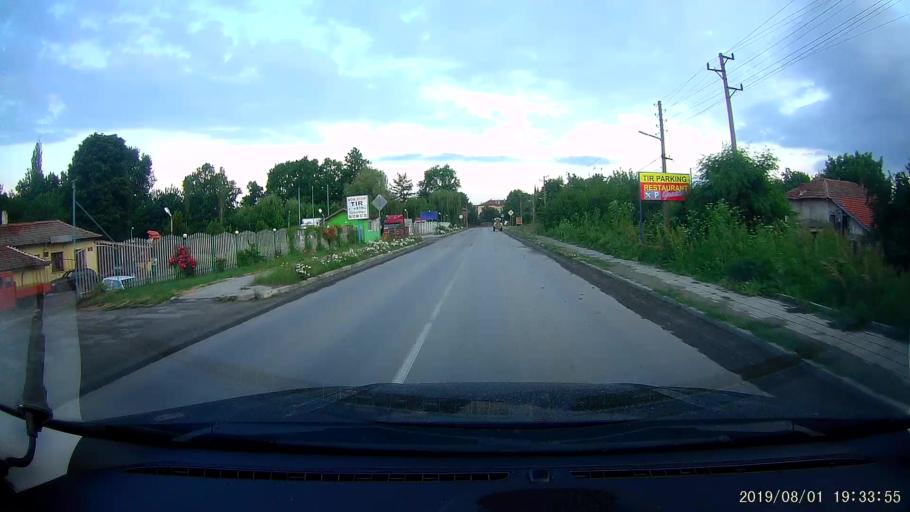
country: BG
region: Burgas
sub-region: Obshtina Sungurlare
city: Sungurlare
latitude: 42.7745
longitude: 26.8781
